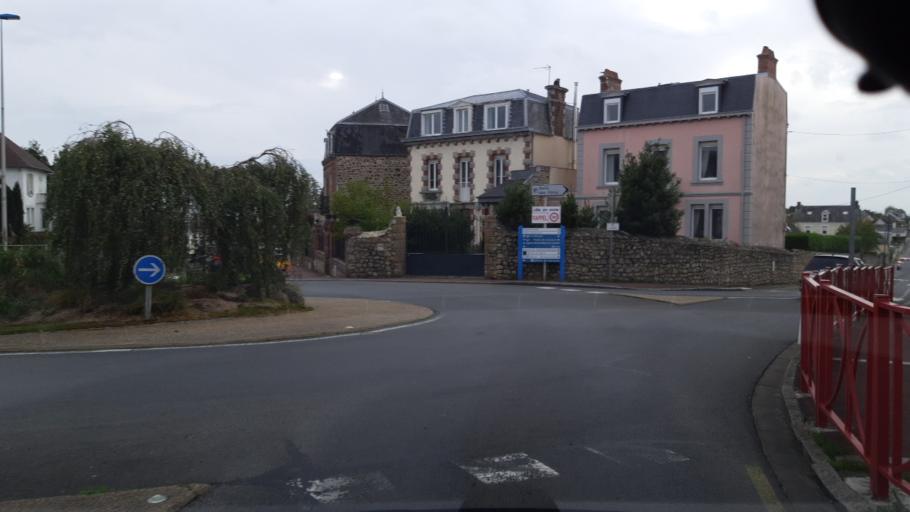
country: FR
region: Lower Normandy
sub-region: Departement de la Manche
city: Donville-les-Bains
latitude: 48.8496
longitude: -1.5746
